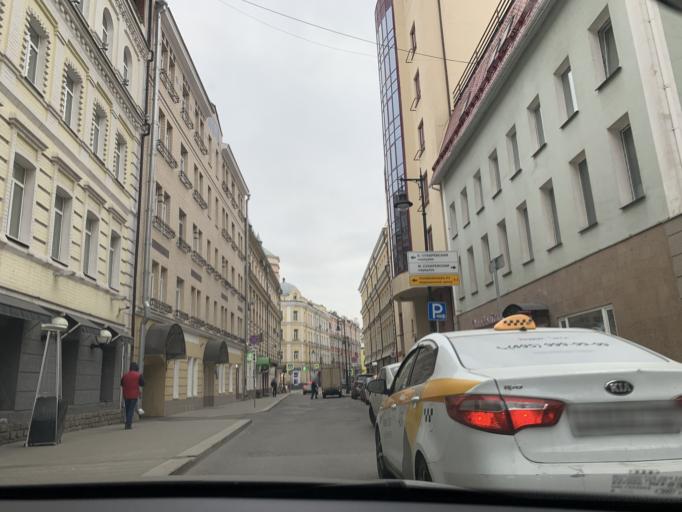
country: RU
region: Moscow
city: Moscow
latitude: 55.7713
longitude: 37.6253
